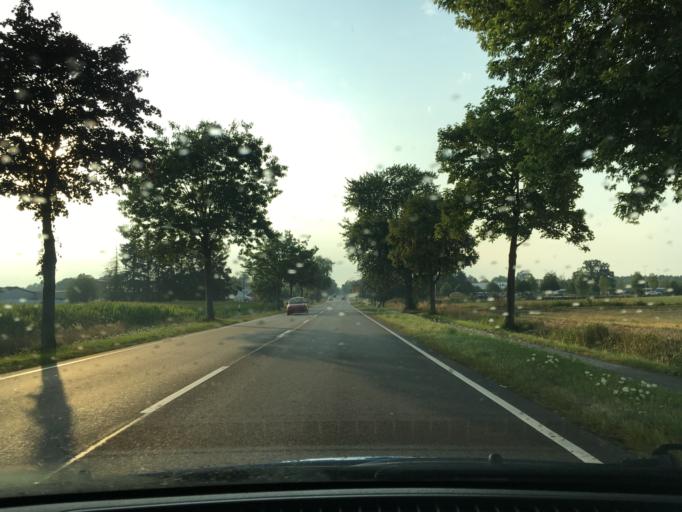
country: DE
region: Lower Saxony
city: Celle
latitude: 52.6495
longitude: 10.0704
